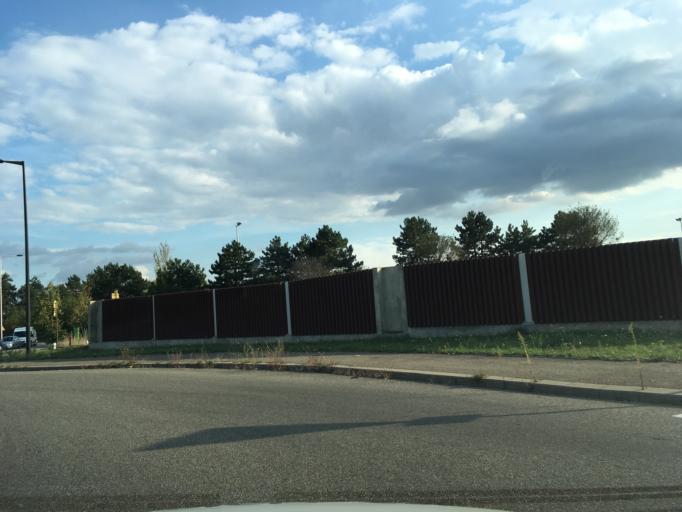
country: FR
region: Alsace
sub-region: Departement du Haut-Rhin
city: Colmar
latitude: 48.0921
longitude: 7.3481
